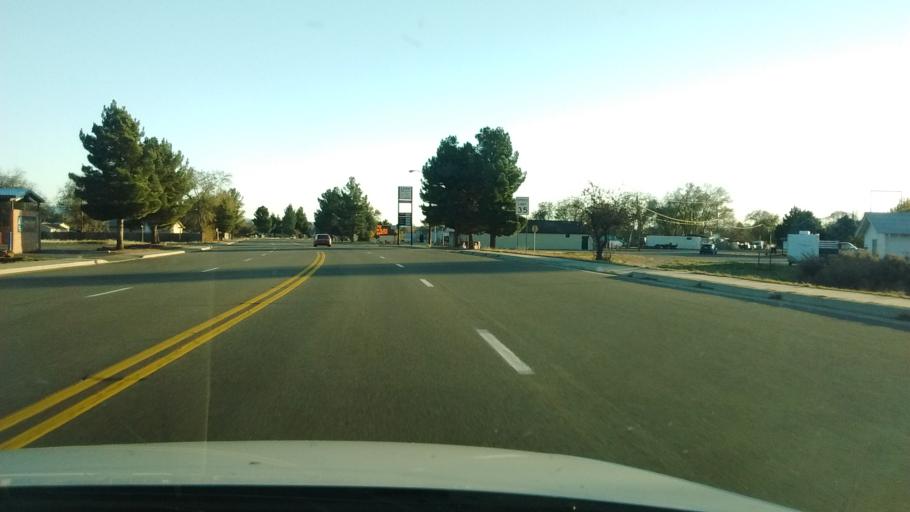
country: US
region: Arizona
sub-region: Coconino County
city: Fredonia
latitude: 36.9565
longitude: -112.5270
